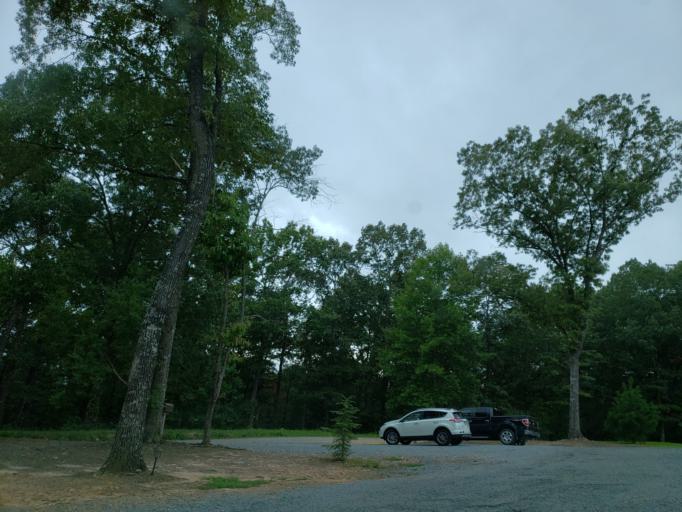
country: US
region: Georgia
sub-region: Gilmer County
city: Ellijay
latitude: 34.6057
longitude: -84.5698
